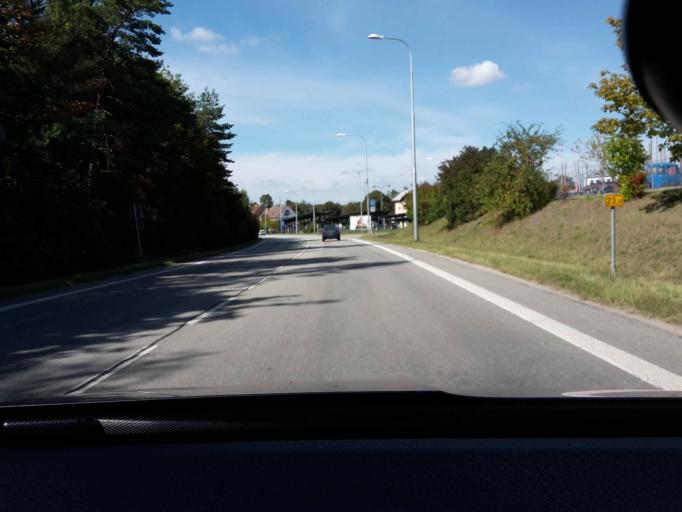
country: CZ
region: Jihocesky
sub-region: Okres Jindrichuv Hradec
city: Jindrichuv Hradec
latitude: 49.1532
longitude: 15.0072
